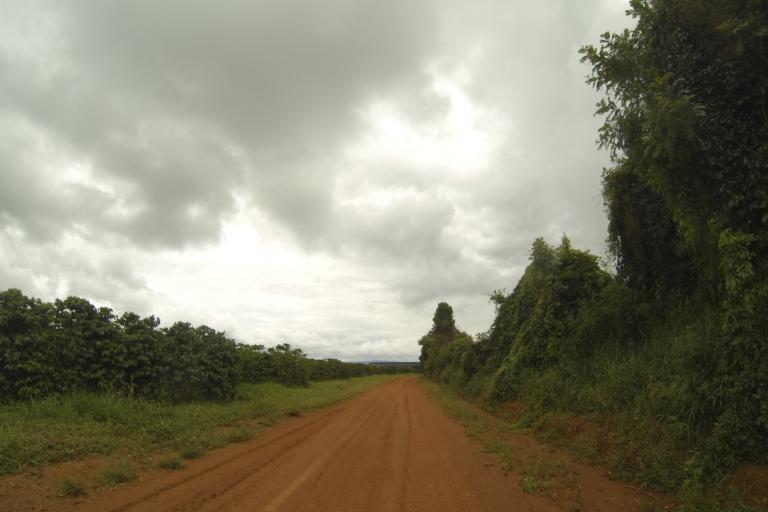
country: BR
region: Minas Gerais
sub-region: Ibia
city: Ibia
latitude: -19.7265
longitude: -46.5908
